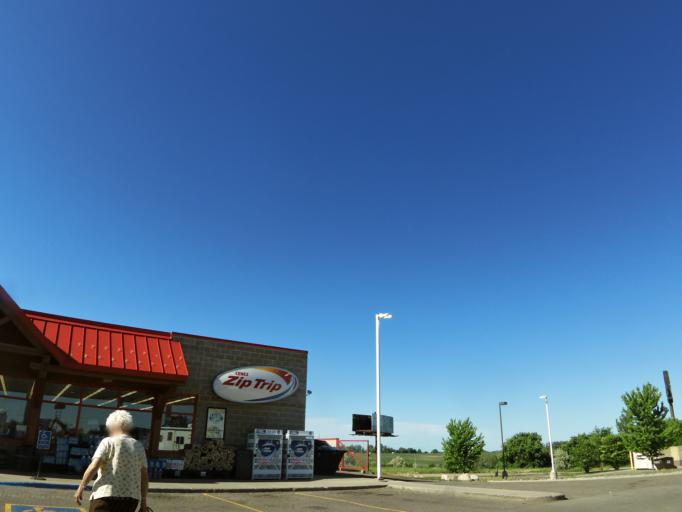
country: US
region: Minnesota
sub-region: Otter Tail County
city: Fergus Falls
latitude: 46.2889
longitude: -96.1176
